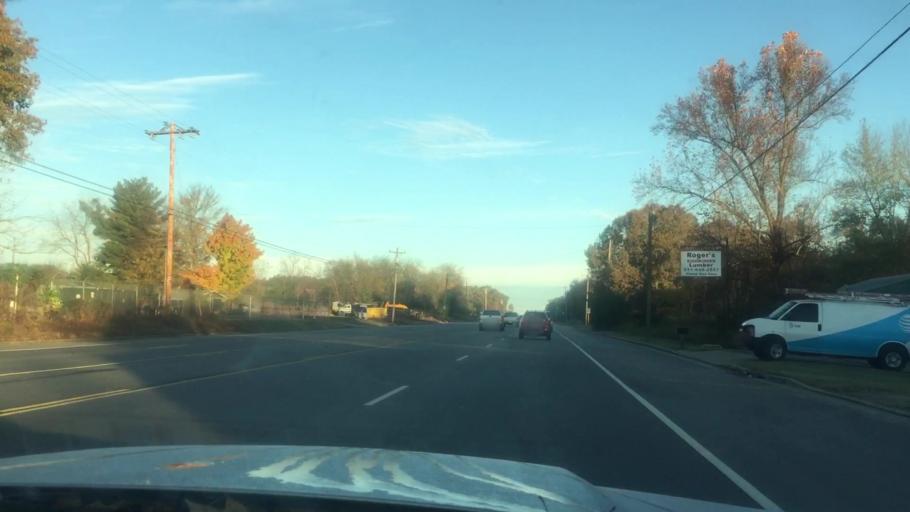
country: US
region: Tennessee
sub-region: Franklin County
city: Estill Springs
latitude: 35.2843
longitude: -86.1403
